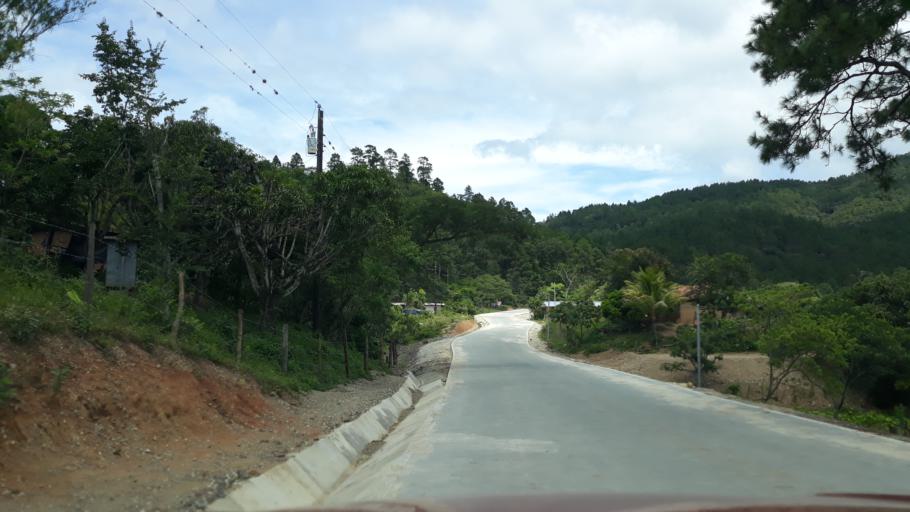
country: HN
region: El Paraiso
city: Santa Cruz
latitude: 13.7411
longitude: -86.6265
